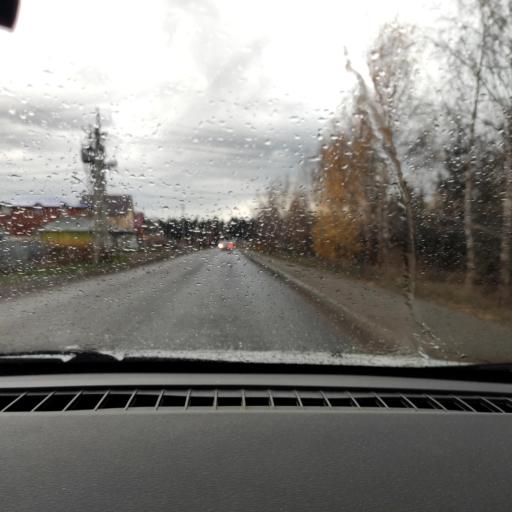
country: RU
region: Perm
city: Kultayevo
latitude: 57.8986
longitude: 55.9620
